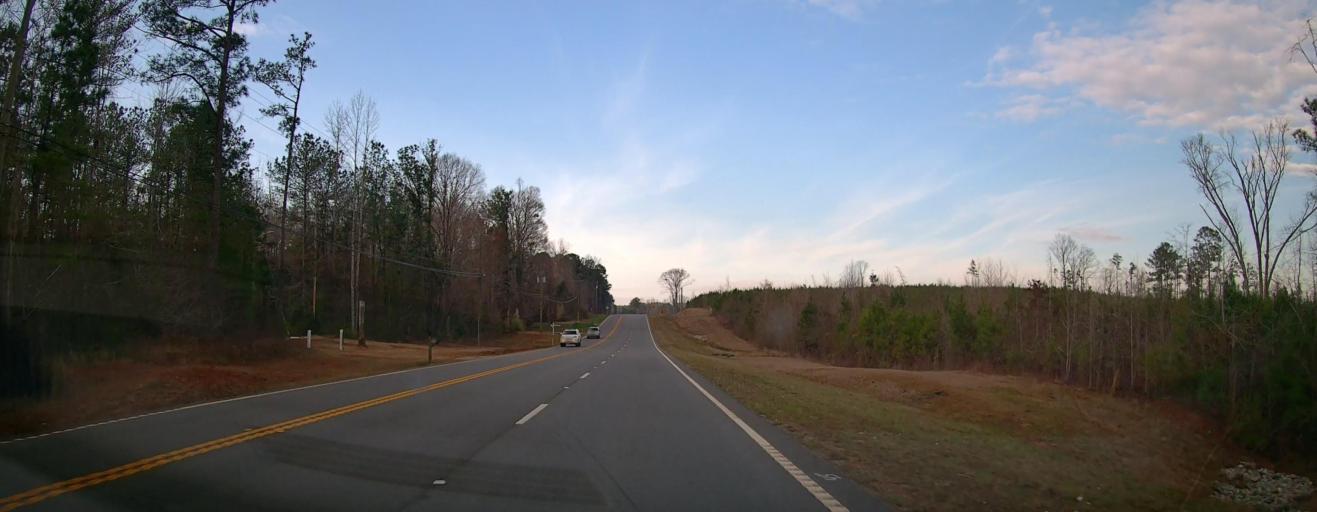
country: US
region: Georgia
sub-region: Harris County
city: Hamilton
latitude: 32.7209
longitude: -84.8736
